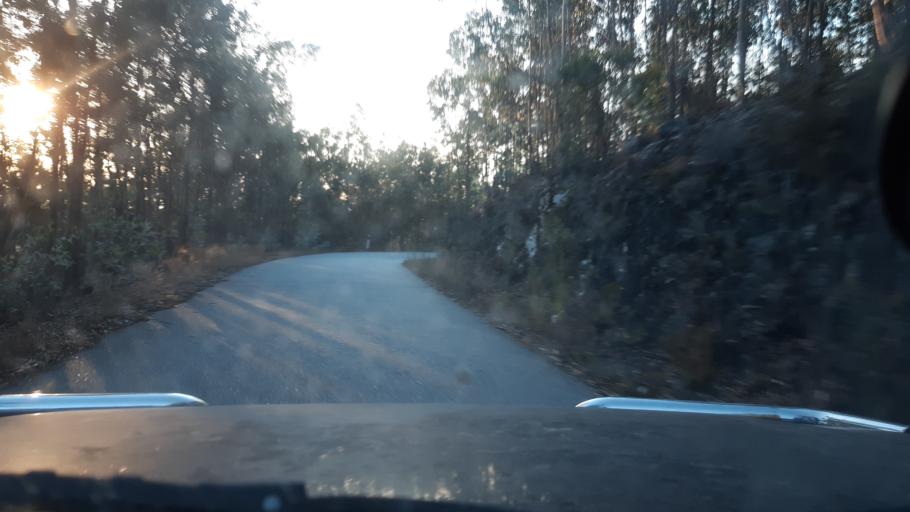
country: PT
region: Aveiro
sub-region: Agueda
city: Aguada de Cima
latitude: 40.5558
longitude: -8.2910
